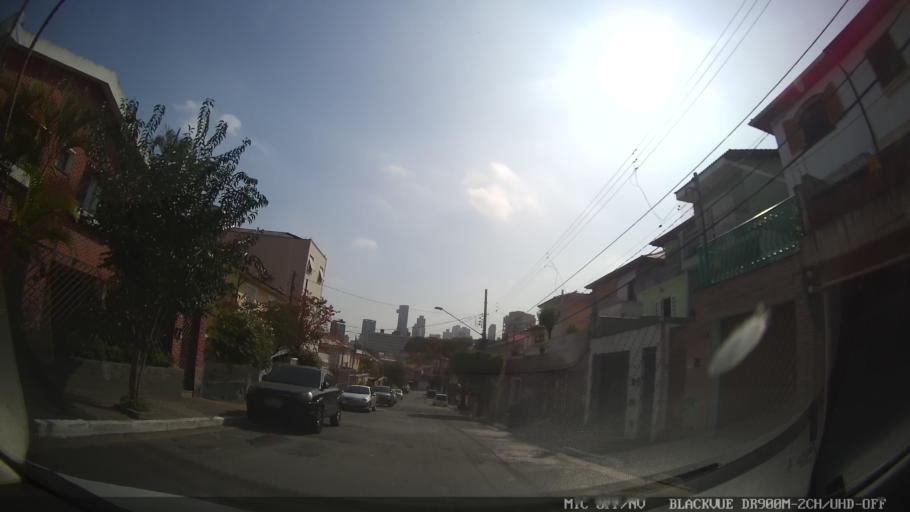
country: BR
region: Sao Paulo
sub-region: Sao Paulo
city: Sao Paulo
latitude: -23.4988
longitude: -46.6168
